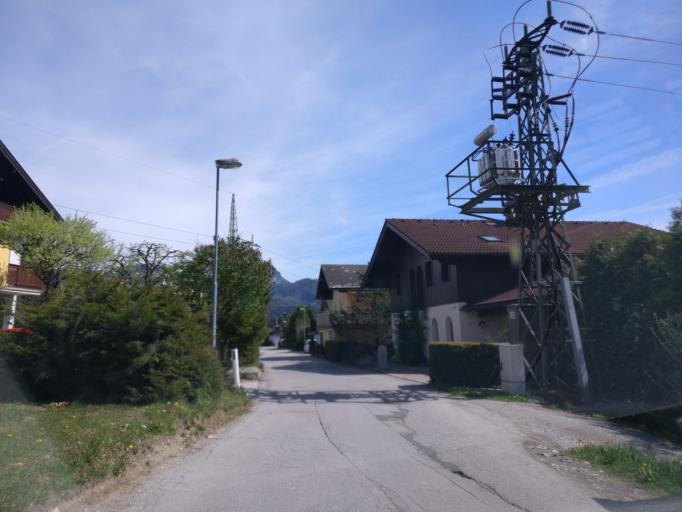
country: AT
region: Salzburg
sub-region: Politischer Bezirk Hallein
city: Kuchl
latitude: 47.6385
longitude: 13.1425
